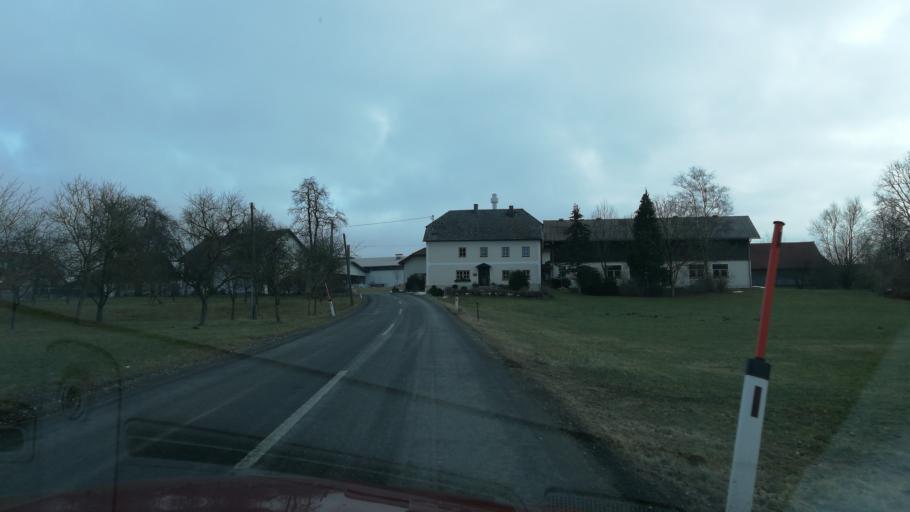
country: AT
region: Upper Austria
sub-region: Politischer Bezirk Vocklabruck
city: Wolfsegg am Hausruck
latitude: 48.1736
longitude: 13.6891
